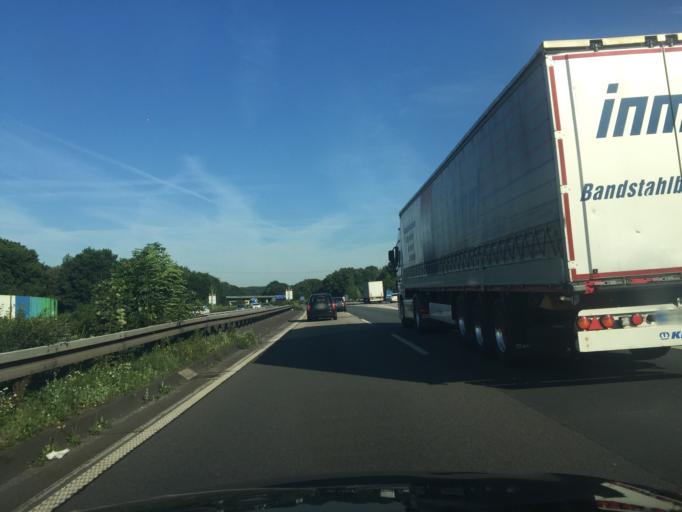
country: DE
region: North Rhine-Westphalia
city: Schwerte
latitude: 51.4300
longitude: 7.5393
